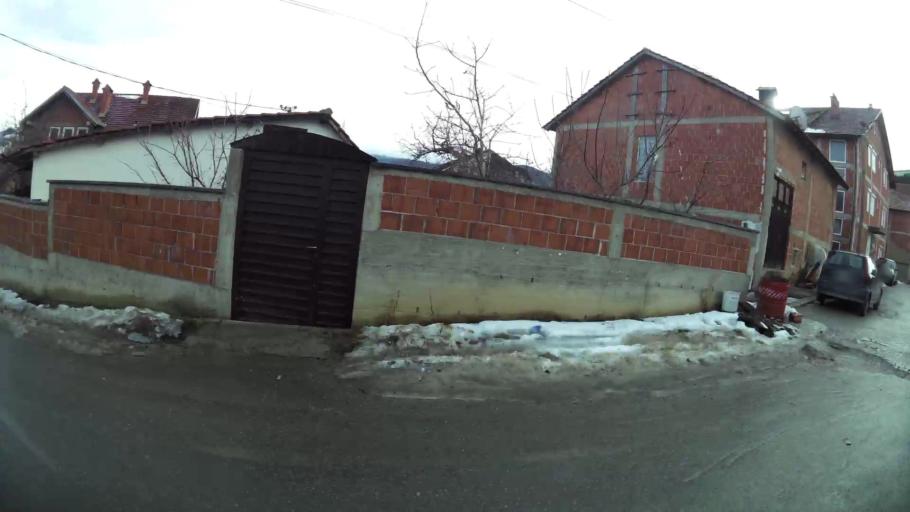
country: XK
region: Pristina
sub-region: Komuna e Prishtines
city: Pristina
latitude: 42.6724
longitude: 21.1837
